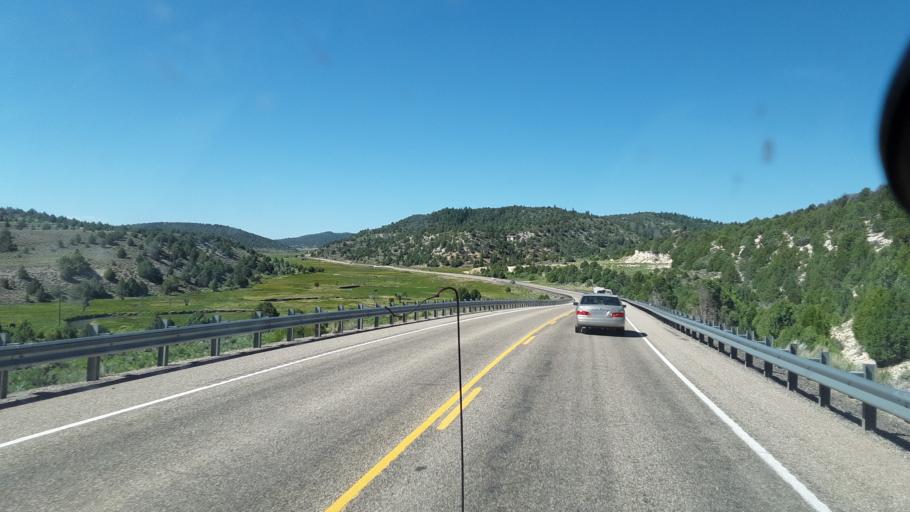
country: US
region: Utah
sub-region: Garfield County
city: Panguitch
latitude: 37.5910
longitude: -112.4742
